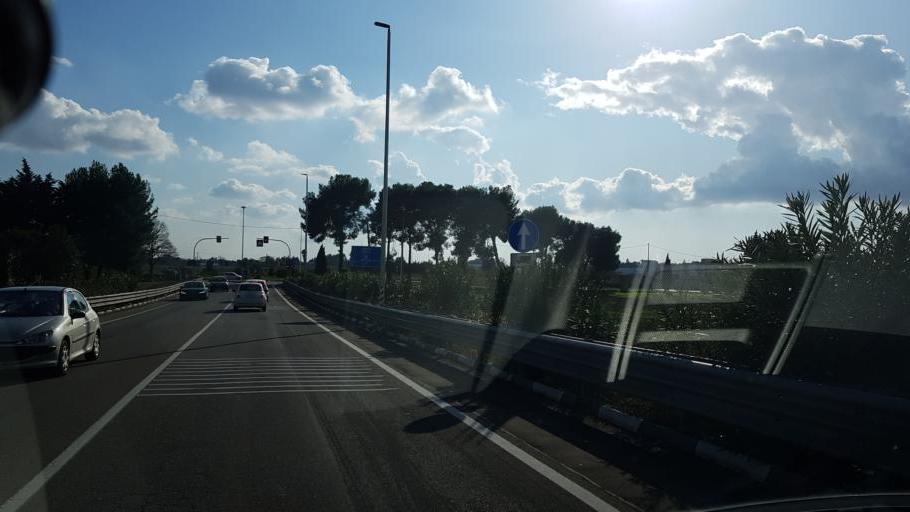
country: IT
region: Apulia
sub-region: Provincia di Lecce
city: Salice Salentino
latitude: 40.3858
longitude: 17.9702
